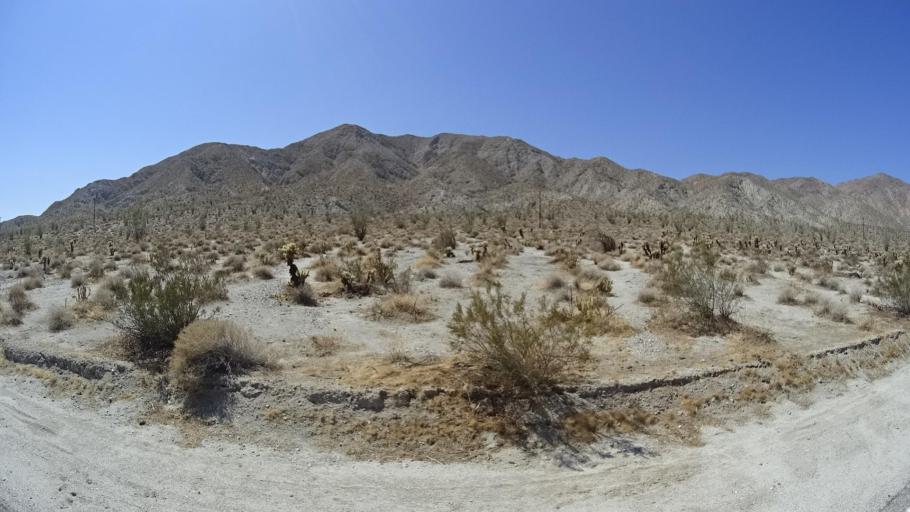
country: US
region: California
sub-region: San Diego County
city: Pine Valley
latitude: 32.9482
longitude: -116.2827
